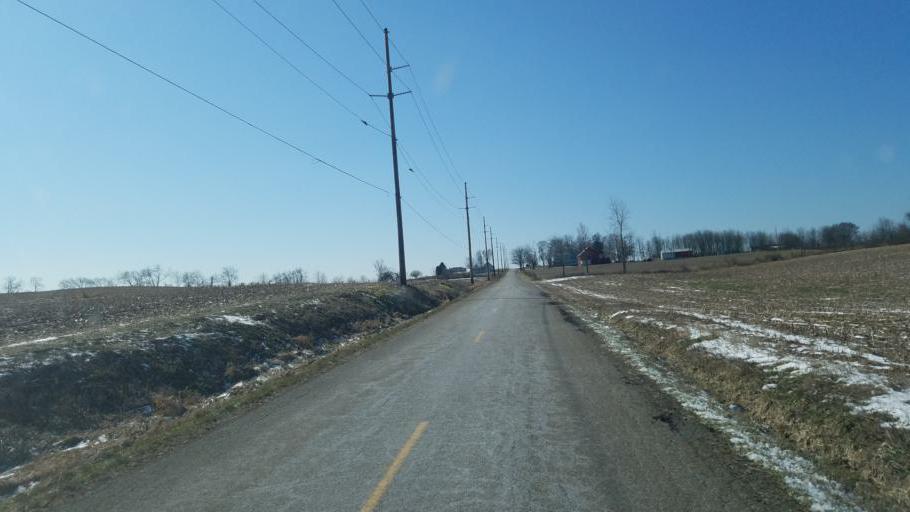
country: US
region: Ohio
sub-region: Licking County
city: Utica
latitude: 40.2916
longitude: -82.4741
